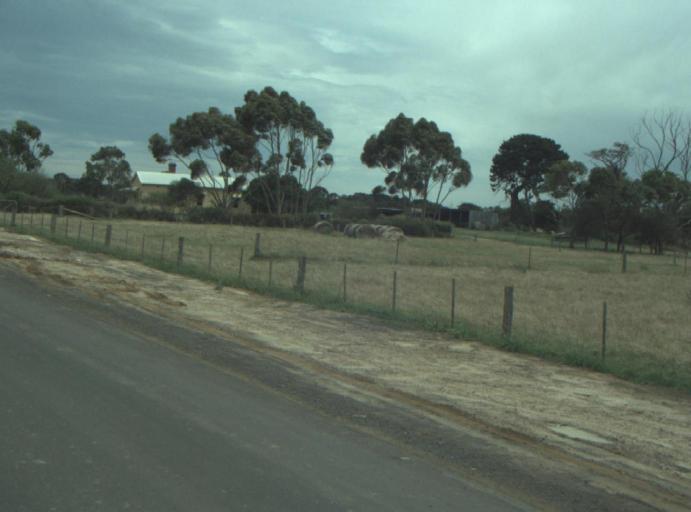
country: AU
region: Victoria
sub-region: Greater Geelong
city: Leopold
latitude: -38.1999
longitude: 144.4529
